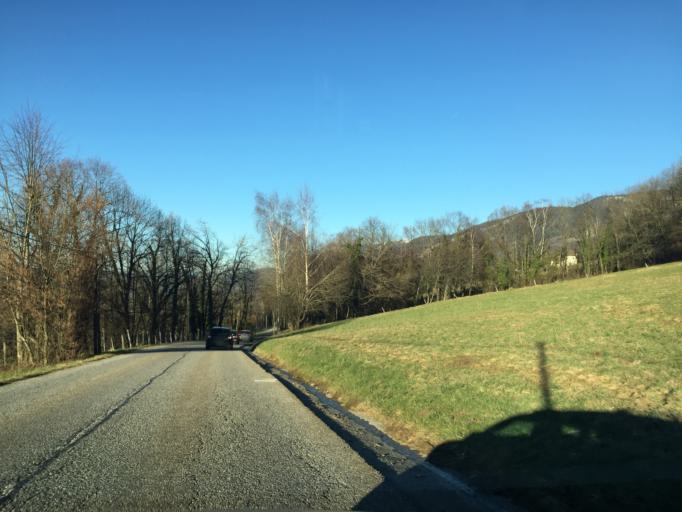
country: FR
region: Rhone-Alpes
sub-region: Departement de la Savoie
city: Mouxy
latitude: 45.7040
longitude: 5.9694
